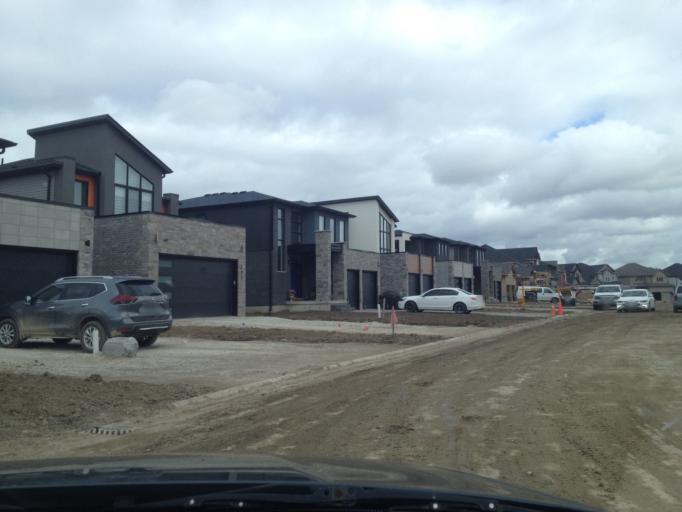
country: CA
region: Ontario
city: London
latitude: 43.0194
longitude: -81.3348
